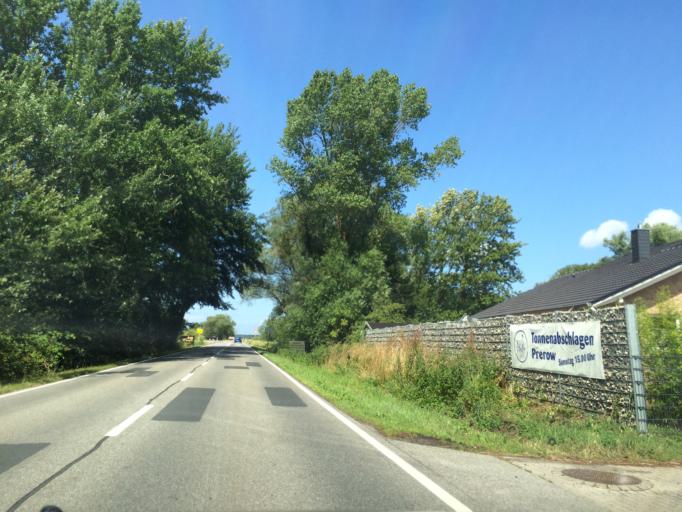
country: DE
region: Mecklenburg-Vorpommern
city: Zingst
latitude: 54.4034
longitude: 12.6762
